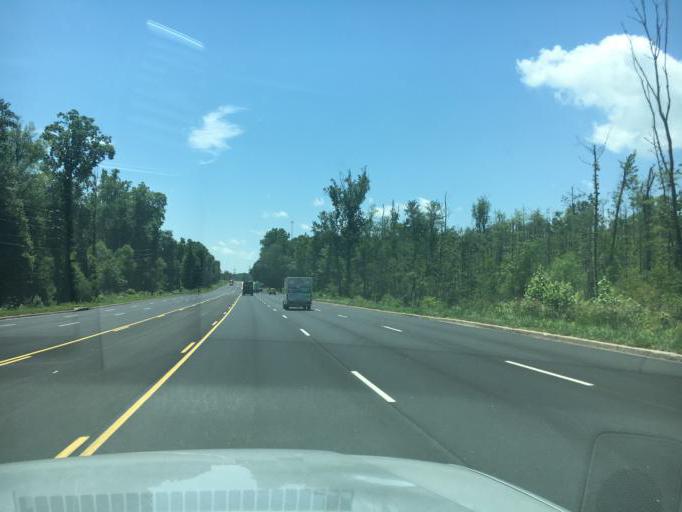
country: US
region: South Carolina
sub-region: Greenville County
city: Berea
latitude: 34.9244
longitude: -82.4566
